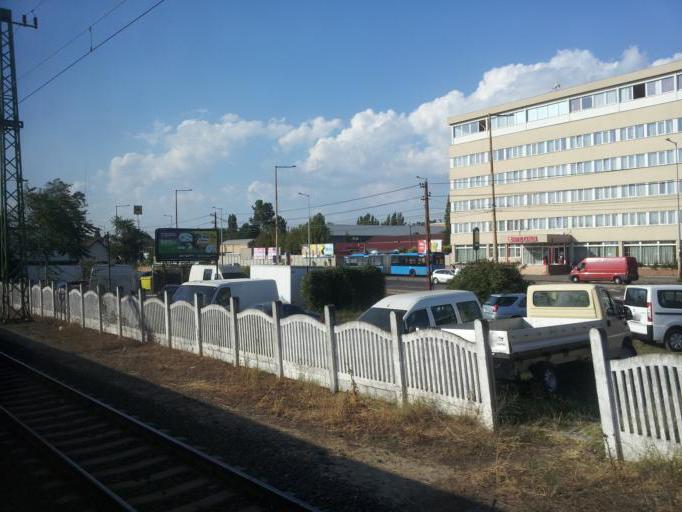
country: HU
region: Budapest
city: Budapest XX. keruelet
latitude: 47.4560
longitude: 19.0853
